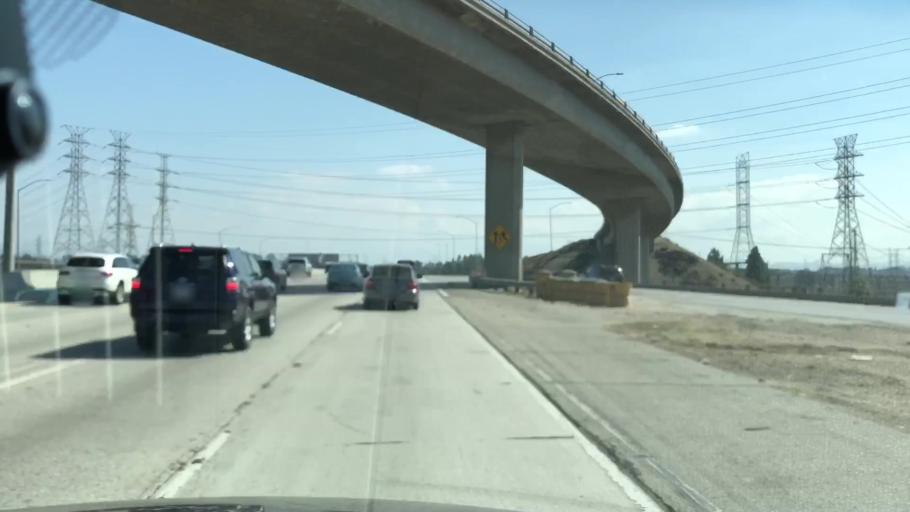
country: US
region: California
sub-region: Los Angeles County
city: San Fernando
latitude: 34.3161
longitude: -118.4905
